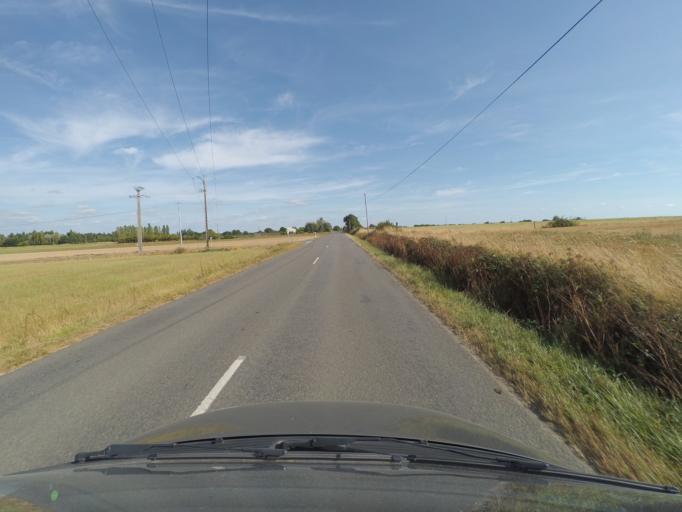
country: FR
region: Pays de la Loire
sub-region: Departement de la Loire-Atlantique
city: Vieillevigne
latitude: 46.9915
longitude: -1.4492
